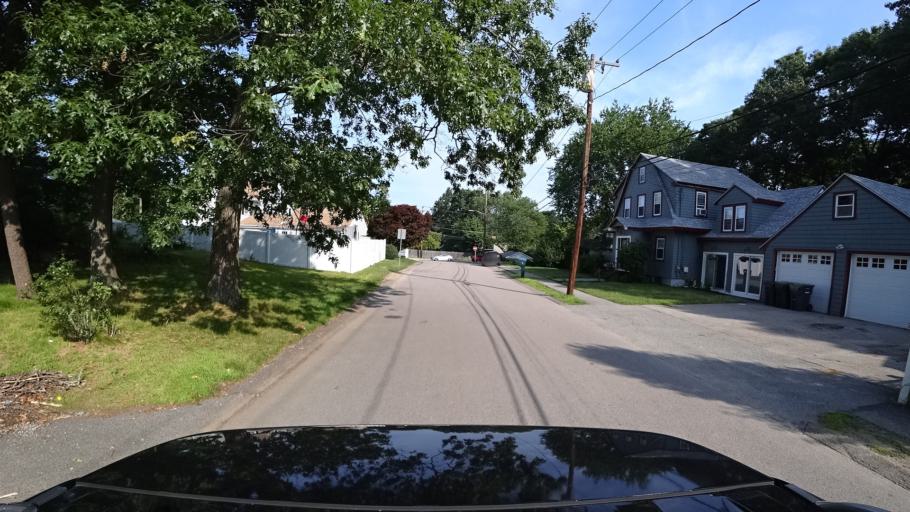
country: US
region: Massachusetts
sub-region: Norfolk County
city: Dedham
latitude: 42.2301
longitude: -71.1597
